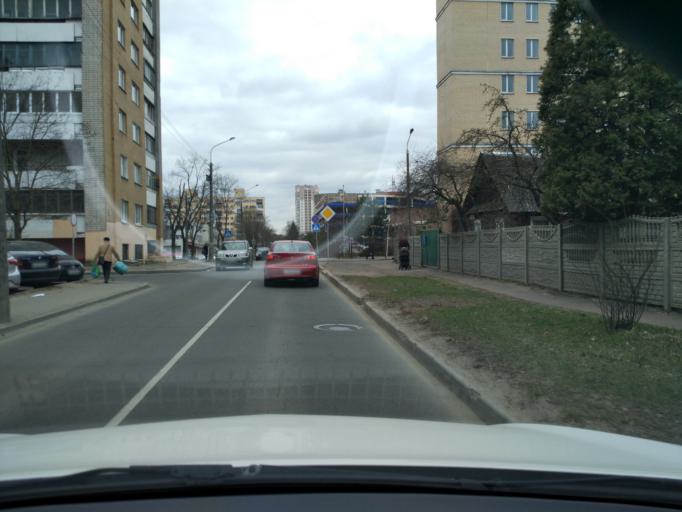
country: BY
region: Minsk
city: Minsk
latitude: 53.9415
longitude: 27.6004
